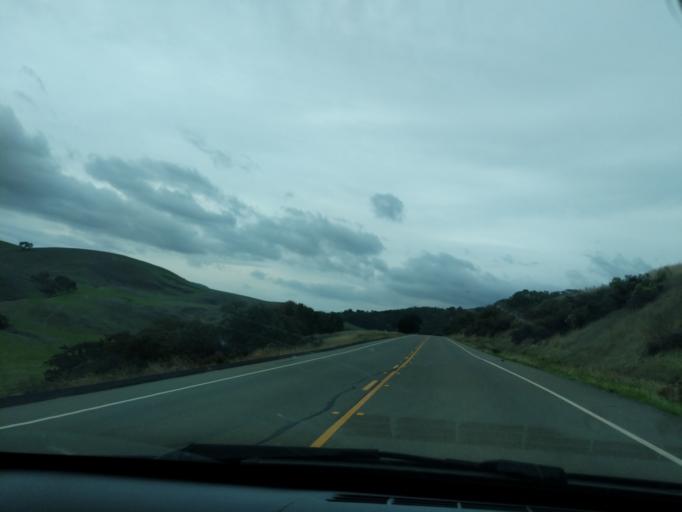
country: US
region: California
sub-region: Monterey County
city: Soledad
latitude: 36.6196
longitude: -121.2192
